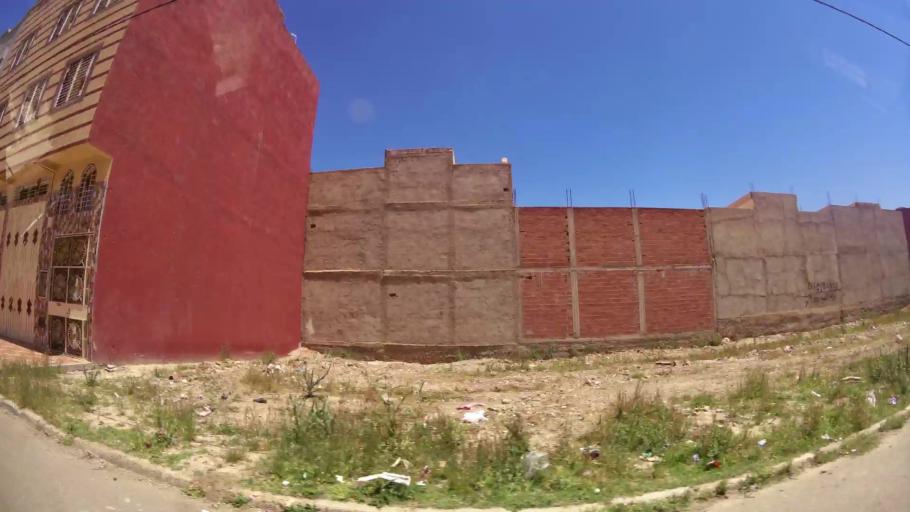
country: MA
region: Oriental
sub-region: Oujda-Angad
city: Oujda
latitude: 34.6764
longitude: -1.8627
